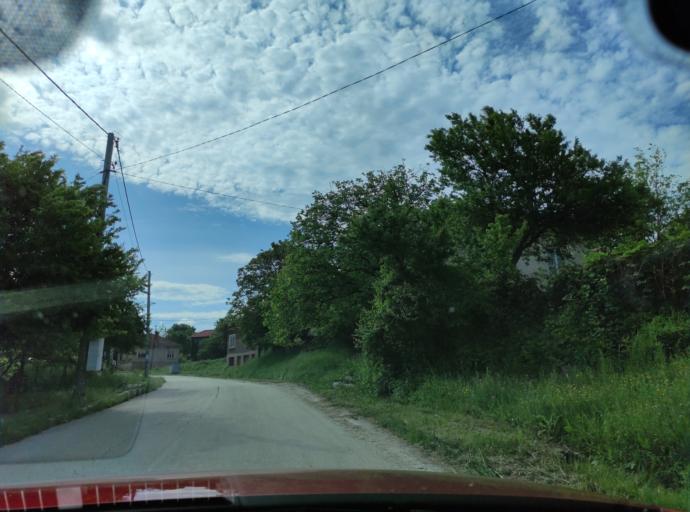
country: BG
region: Vidin
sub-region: Obshtina Belogradchik
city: Belogradchik
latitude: 43.5147
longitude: 22.7365
